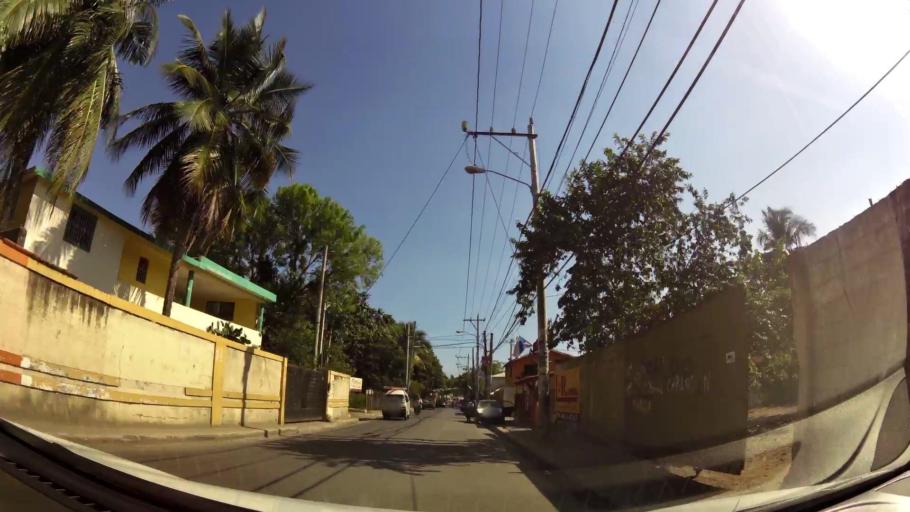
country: DO
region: Santo Domingo
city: Santo Domingo Oeste
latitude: 18.4716
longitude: -69.9994
